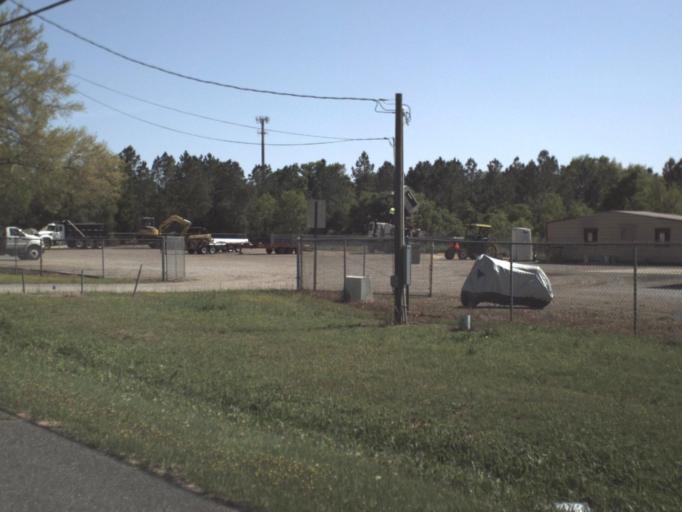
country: US
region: Florida
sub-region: Escambia County
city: Bellview
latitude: 30.4817
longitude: -87.3117
